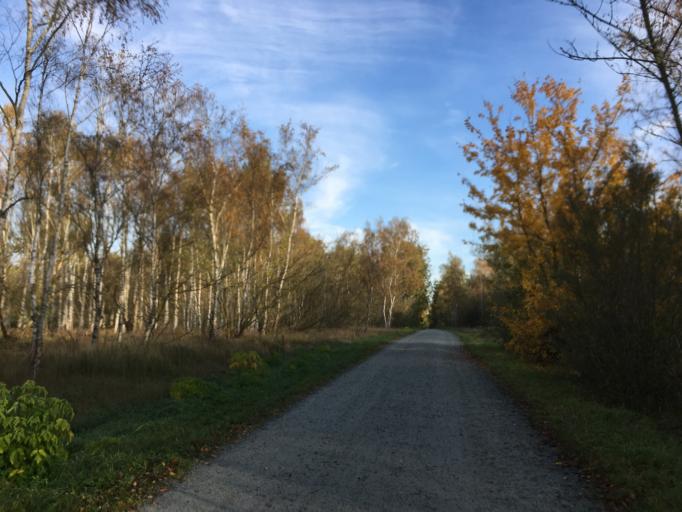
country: DE
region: Berlin
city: Buch
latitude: 52.6589
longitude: 13.4834
